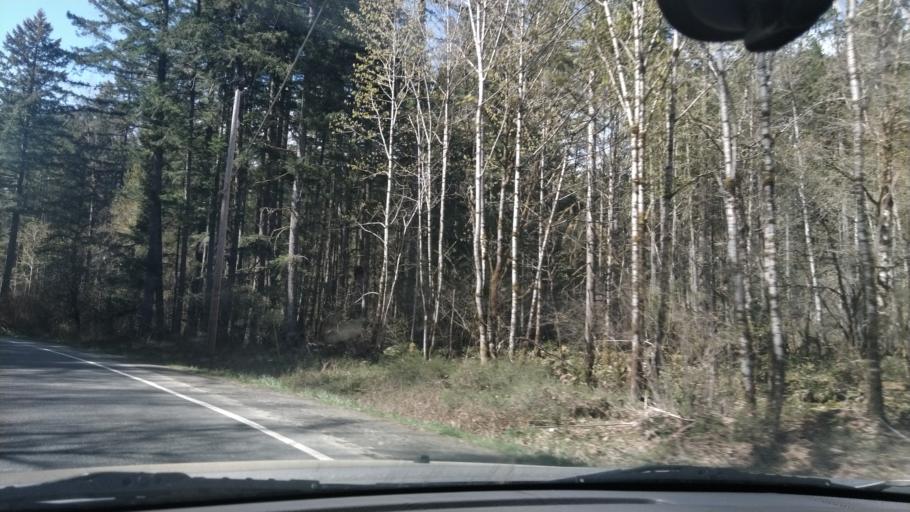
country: CA
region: British Columbia
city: Courtenay
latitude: 49.6957
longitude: -125.0575
